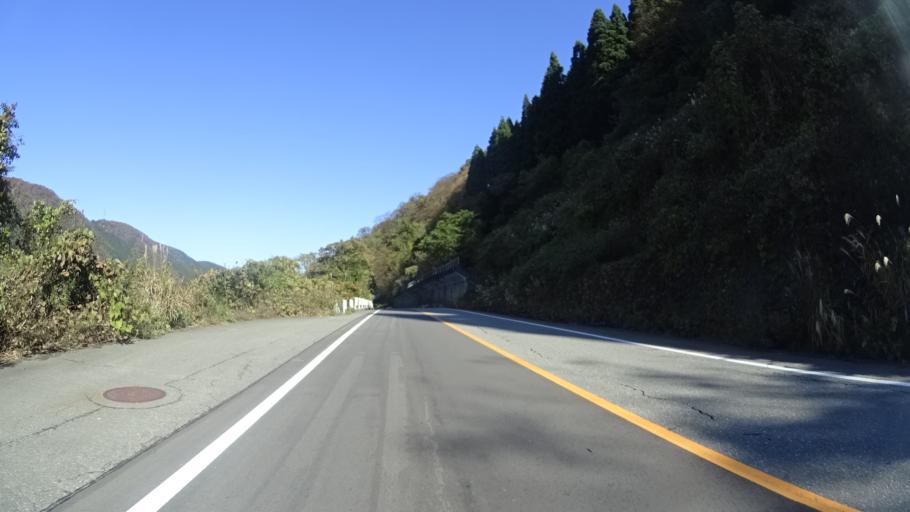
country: JP
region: Ishikawa
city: Tsurugi-asahimachi
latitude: 36.4059
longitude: 136.6329
